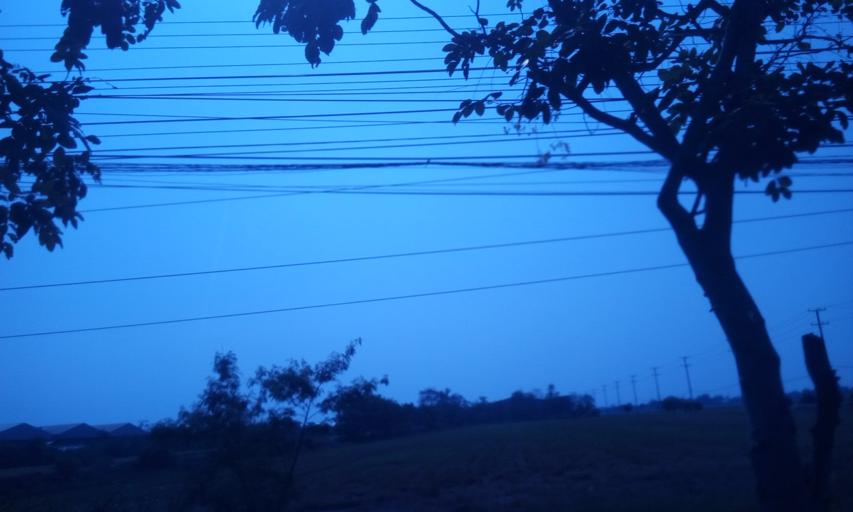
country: TH
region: Nonthaburi
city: Sai Noi
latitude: 14.0330
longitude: 100.3123
